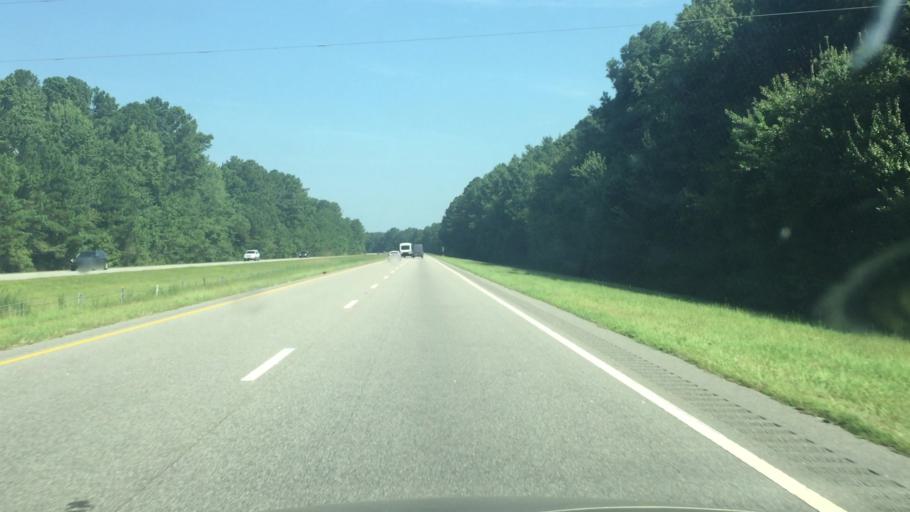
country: US
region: North Carolina
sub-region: Robeson County
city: Lumberton
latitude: 34.5588
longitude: -79.0261
